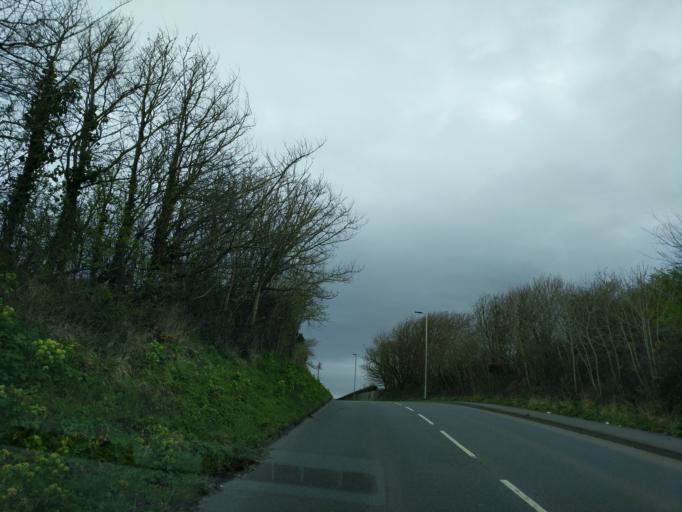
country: GB
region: England
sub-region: Devon
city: Appledore
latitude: 51.0449
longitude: -4.2034
